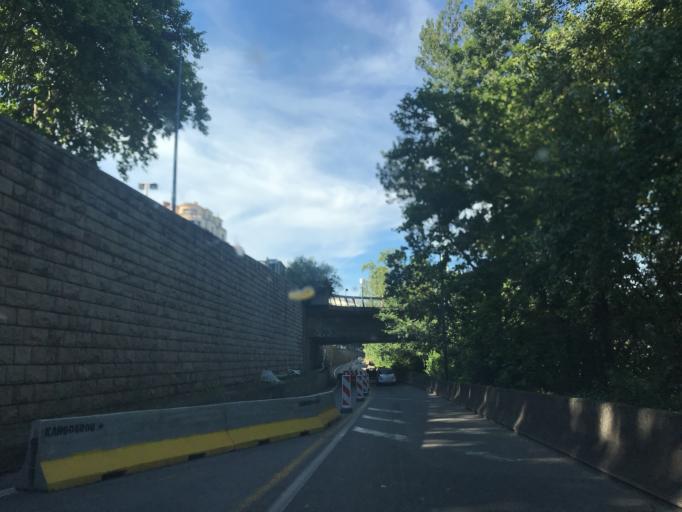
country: FR
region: Rhone-Alpes
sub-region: Departement du Rhone
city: Caluire-et-Cuire
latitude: 45.7782
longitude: 4.8410
